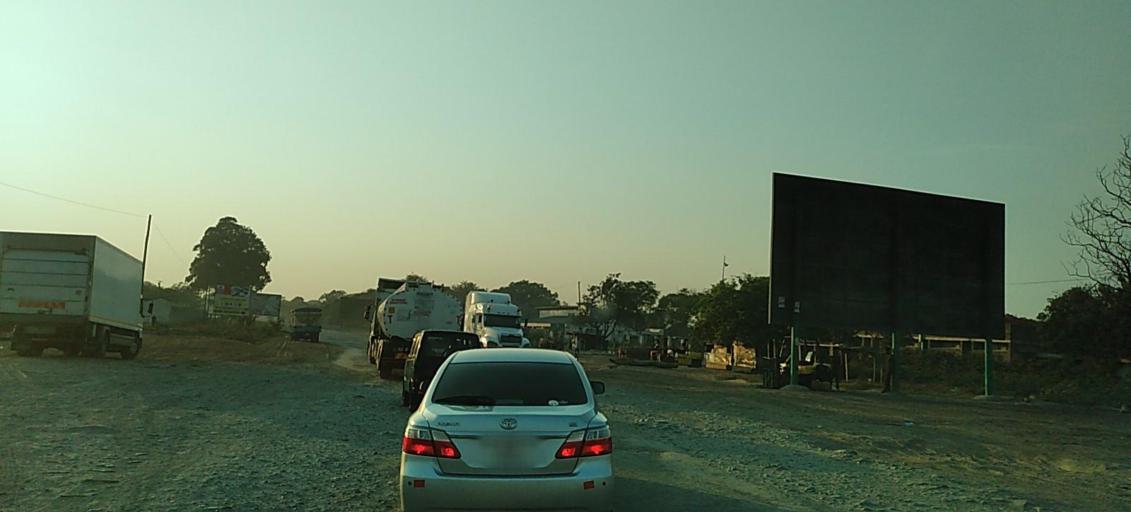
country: ZM
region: Copperbelt
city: Ndola
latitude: -13.0094
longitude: 28.6541
